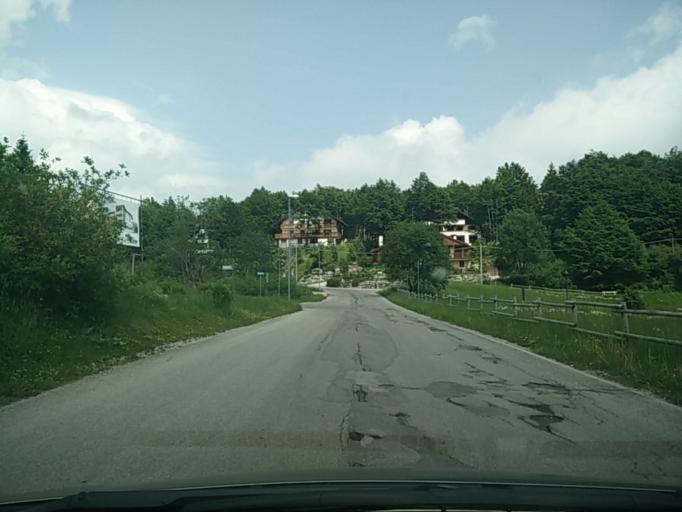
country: IT
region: Friuli Venezia Giulia
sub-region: Provincia di Pordenone
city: Budoia
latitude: 46.1081
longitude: 12.5208
